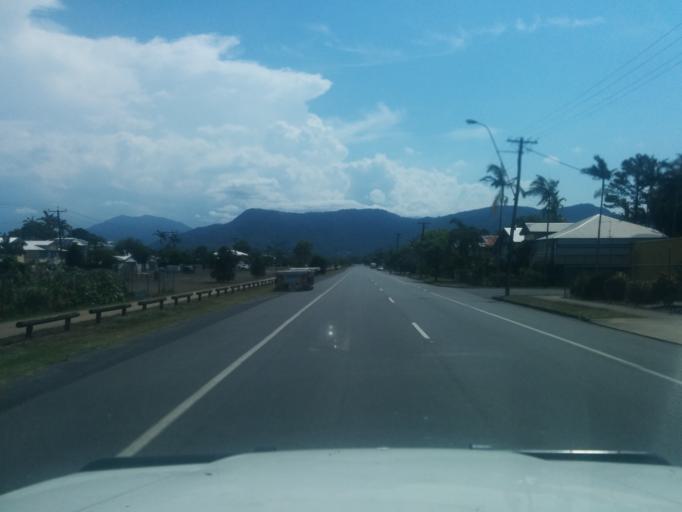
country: AU
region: Queensland
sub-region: Cairns
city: Cairns
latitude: -16.9356
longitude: 145.7619
